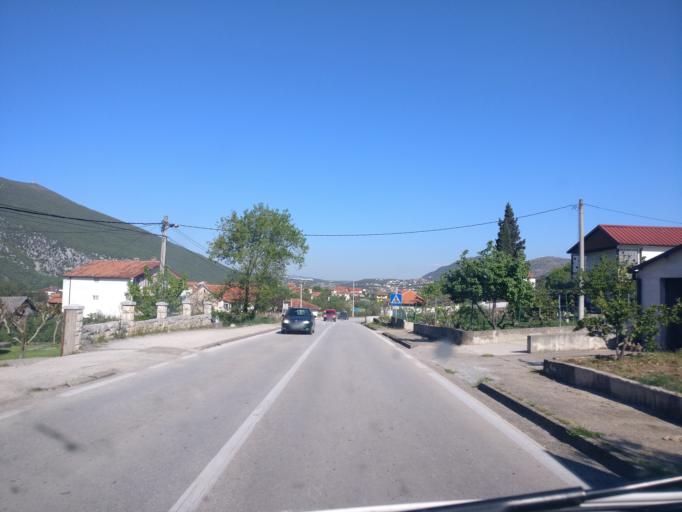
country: BA
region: Federation of Bosnia and Herzegovina
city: Capljina
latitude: 43.1236
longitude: 17.6828
